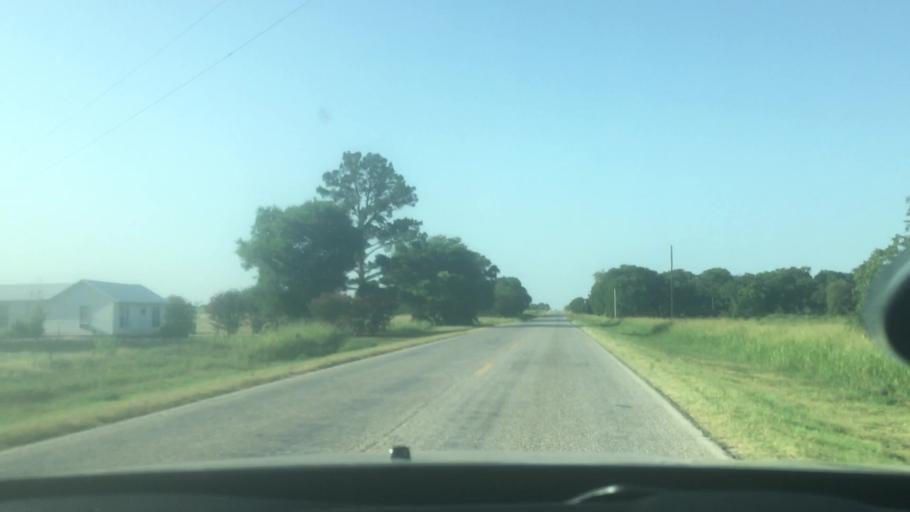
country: US
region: Oklahoma
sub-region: Johnston County
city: Tishomingo
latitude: 34.2924
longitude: -96.4248
